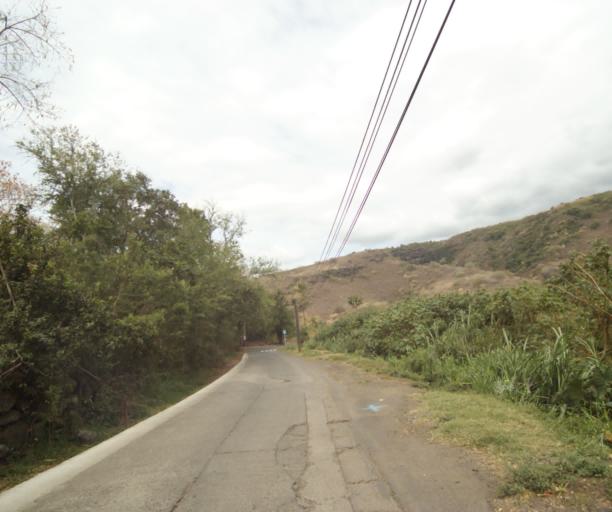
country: RE
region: Reunion
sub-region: Reunion
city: Saint-Paul
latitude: -20.9925
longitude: 55.3069
